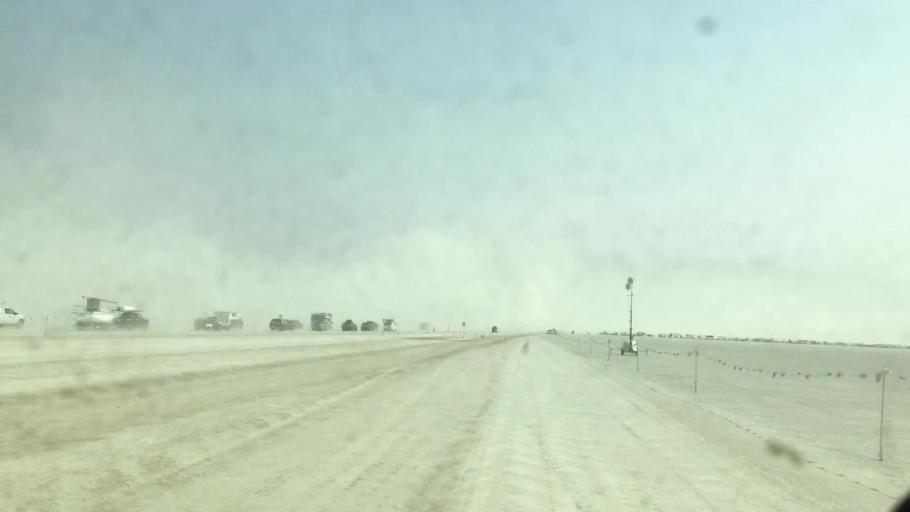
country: US
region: Nevada
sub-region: Pershing County
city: Lovelock
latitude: 40.7606
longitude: -119.2520
